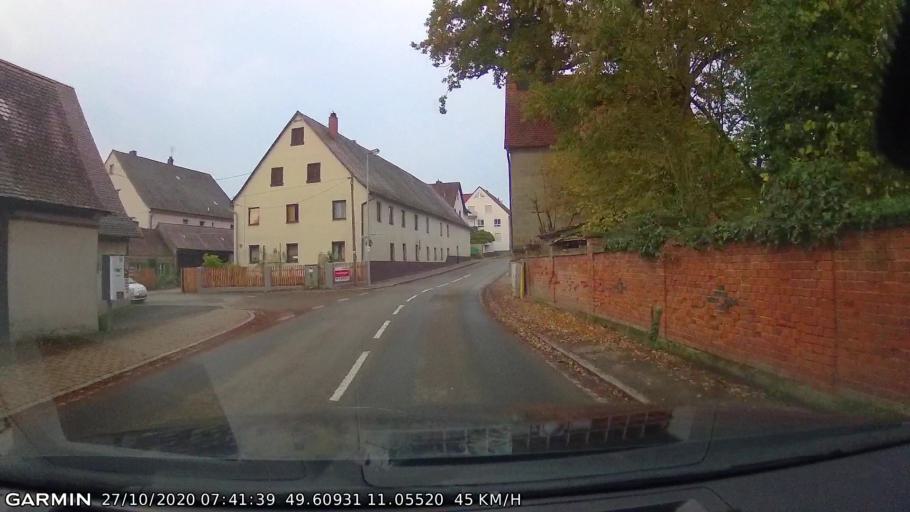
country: DE
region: Bavaria
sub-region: Regierungsbezirk Mittelfranken
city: Spardorf
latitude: 49.6093
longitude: 11.0550
